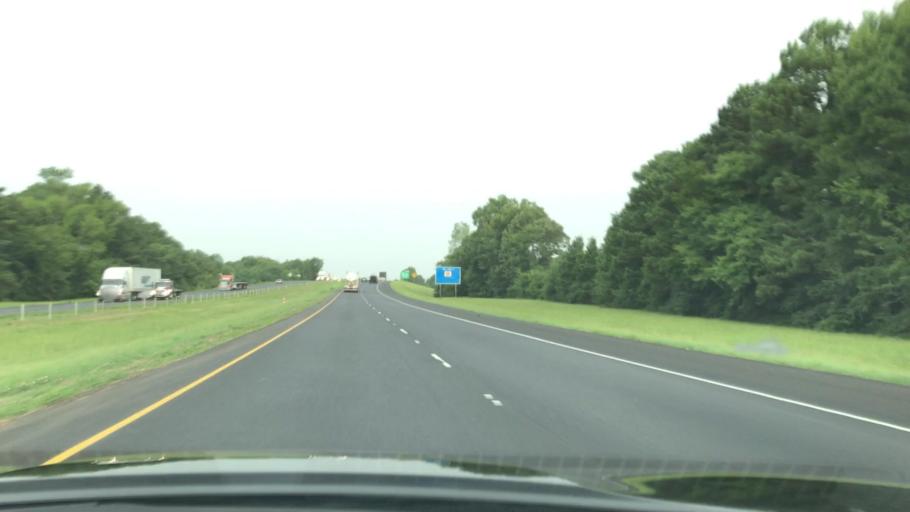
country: US
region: Louisiana
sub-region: Caddo Parish
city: Greenwood
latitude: 32.4443
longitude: -93.9324
